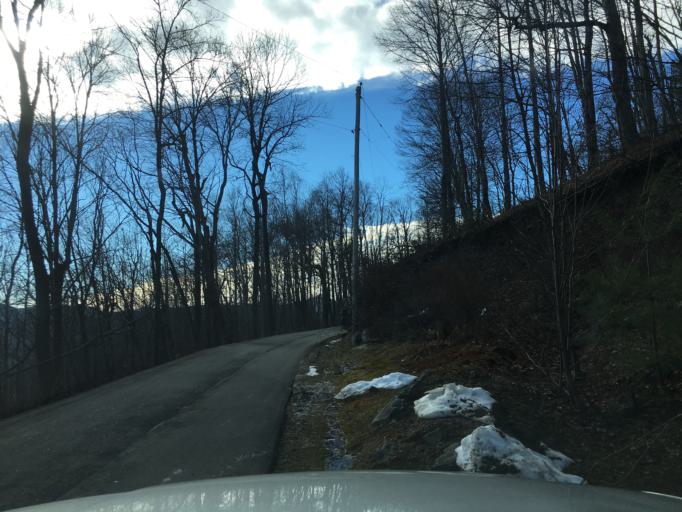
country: US
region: North Carolina
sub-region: Jackson County
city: Cullowhee
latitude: 35.1326
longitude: -83.0032
